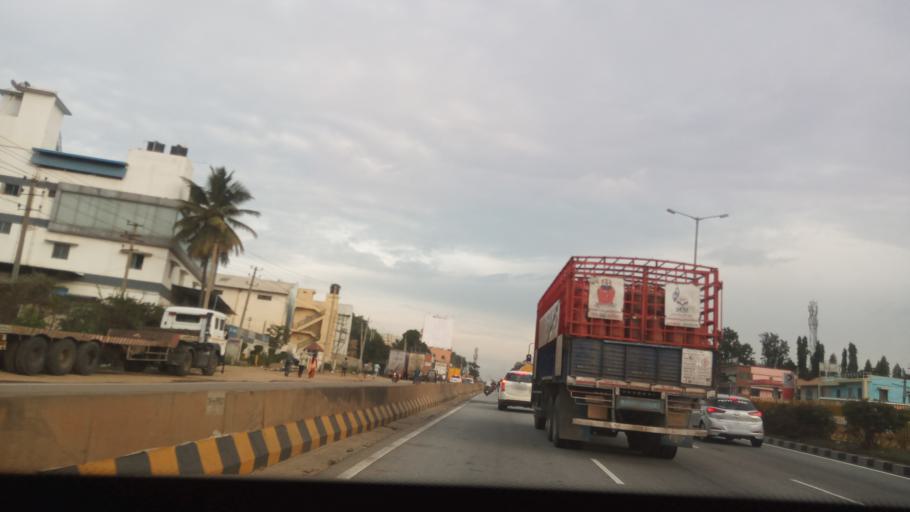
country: IN
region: Karnataka
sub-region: Bangalore Rural
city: Nelamangala
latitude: 13.0626
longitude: 77.4589
